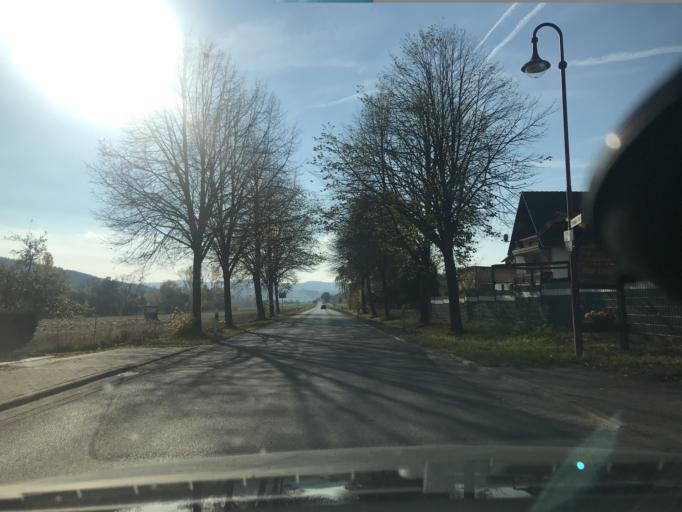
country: DE
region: Hesse
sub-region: Regierungsbezirk Kassel
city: Grossalmerode
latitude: 51.2122
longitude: 9.7938
